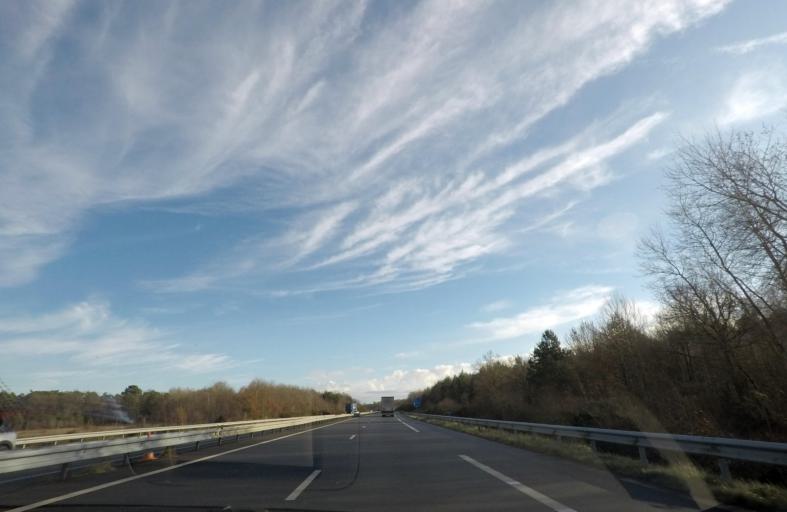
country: FR
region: Centre
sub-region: Departement du Loir-et-Cher
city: Theillay
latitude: 47.2904
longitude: 2.0142
